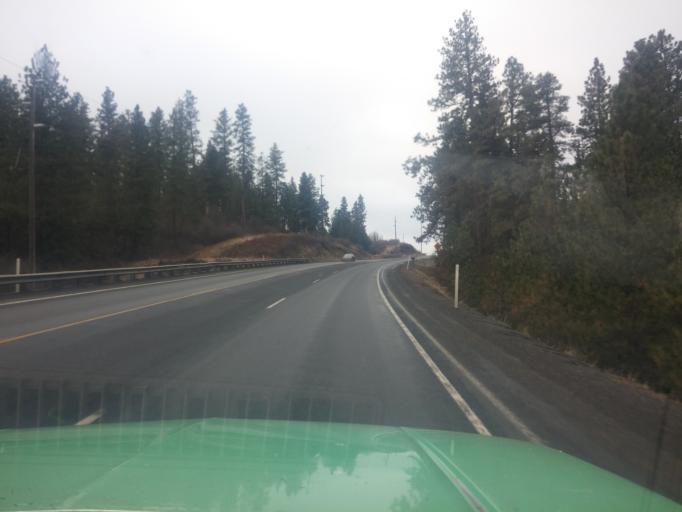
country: US
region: Idaho
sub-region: Latah County
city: Moscow
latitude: 46.8747
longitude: -117.0061
